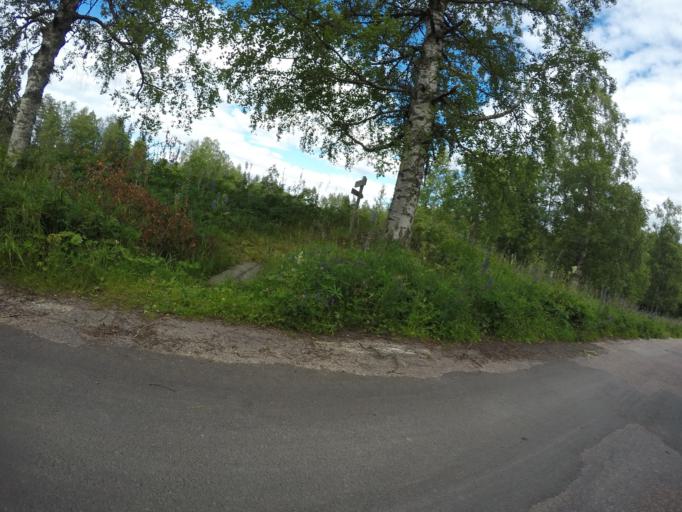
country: SE
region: OErebro
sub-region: Hallefors Kommun
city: Haellefors
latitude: 60.0441
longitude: 14.5049
